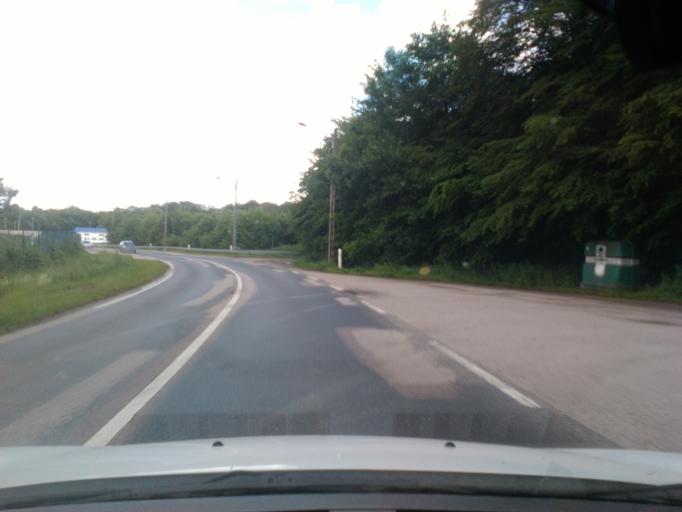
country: FR
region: Lorraine
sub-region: Departement des Vosges
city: Les Forges
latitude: 48.1904
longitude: 6.4030
